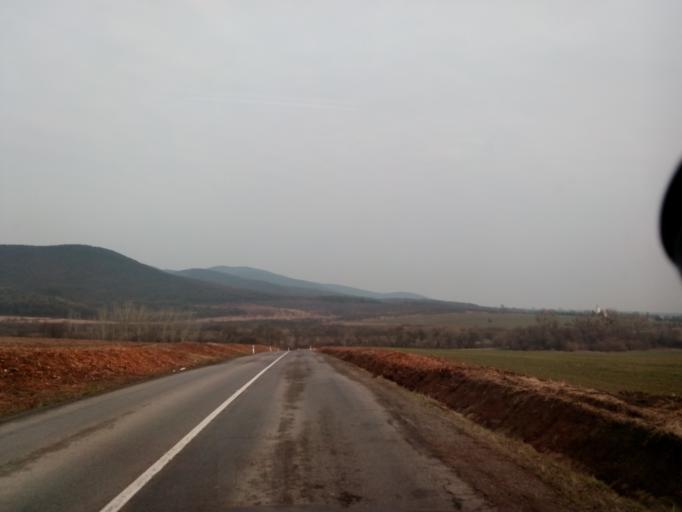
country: SK
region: Kosicky
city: Secovce
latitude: 48.6346
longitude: 21.5549
